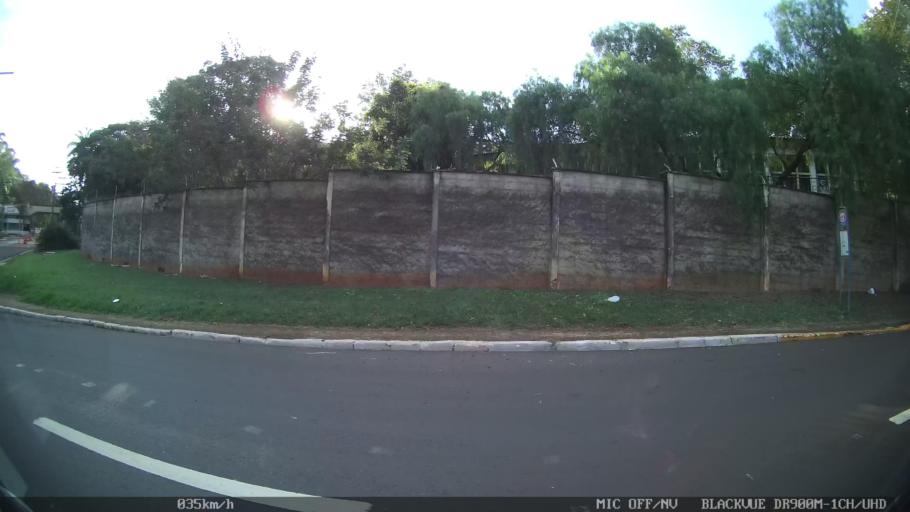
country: BR
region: Sao Paulo
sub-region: Ribeirao Preto
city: Ribeirao Preto
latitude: -21.1724
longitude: -47.8451
